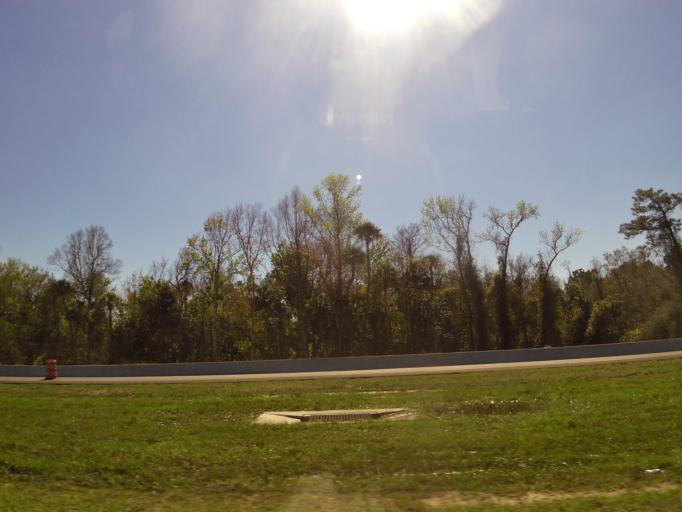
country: US
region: Florida
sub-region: Lake County
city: Mount Plymouth
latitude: 28.8149
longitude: -81.4833
